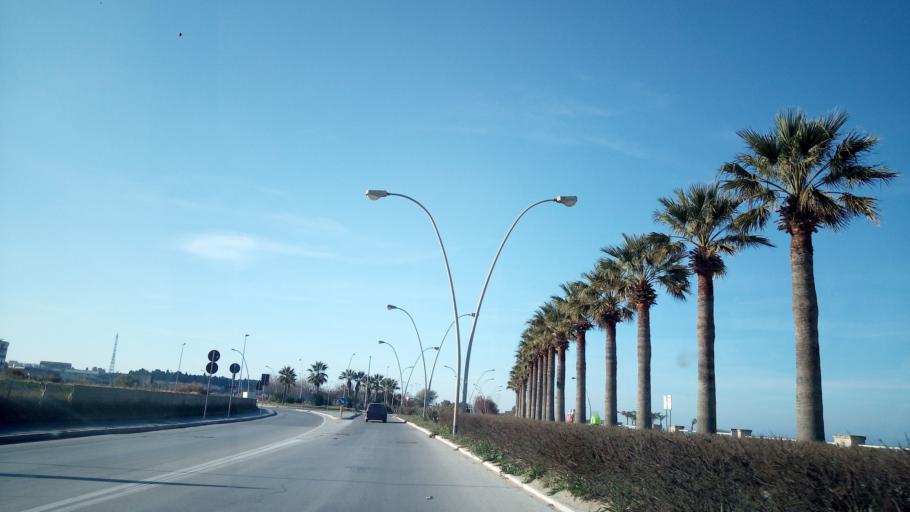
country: IT
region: Apulia
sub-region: Provincia di Barletta - Andria - Trani
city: Barletta
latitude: 41.3253
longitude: 16.2684
